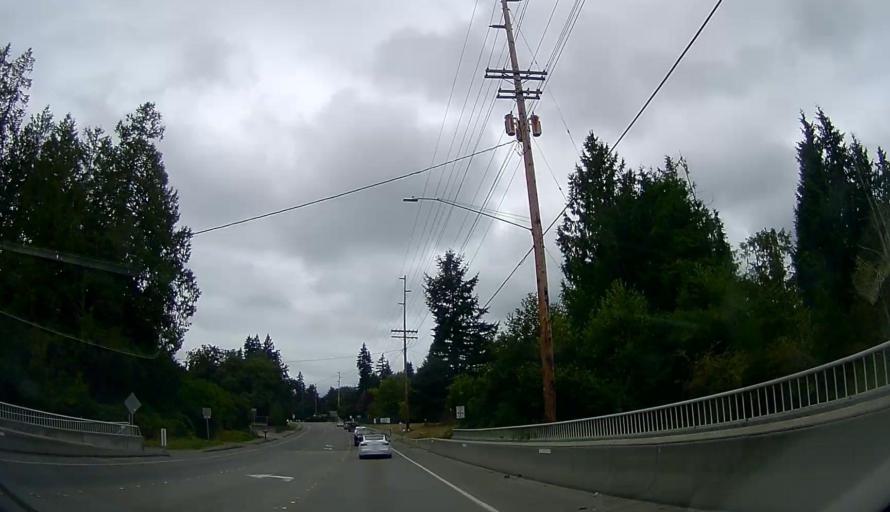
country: US
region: Washington
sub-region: Snohomish County
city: Marysville
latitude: 48.0555
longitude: -122.1976
